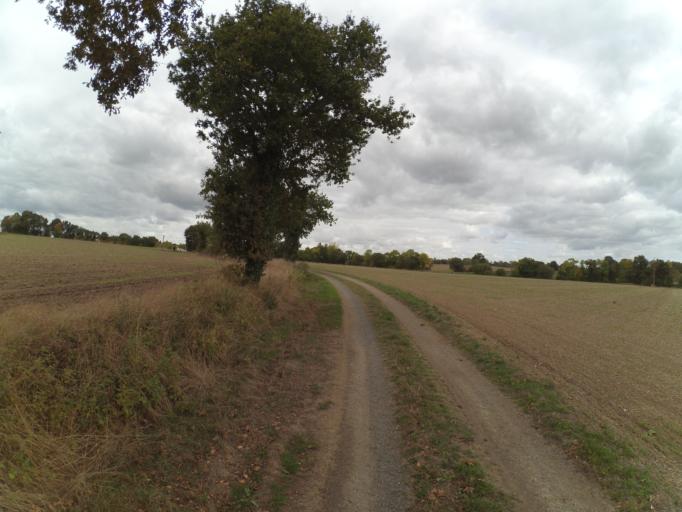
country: FR
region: Pays de la Loire
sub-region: Departement de la Loire-Atlantique
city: Remouille
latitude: 47.0566
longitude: -1.3492
